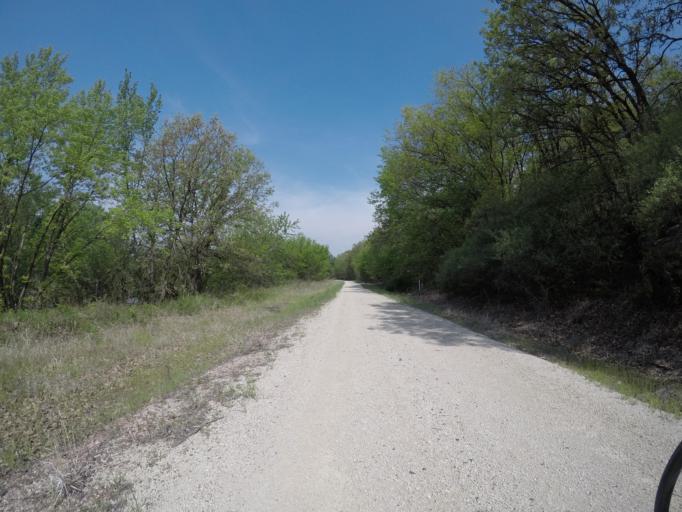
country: US
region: Nebraska
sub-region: Gage County
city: Wymore
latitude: 40.1131
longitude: -96.6259
